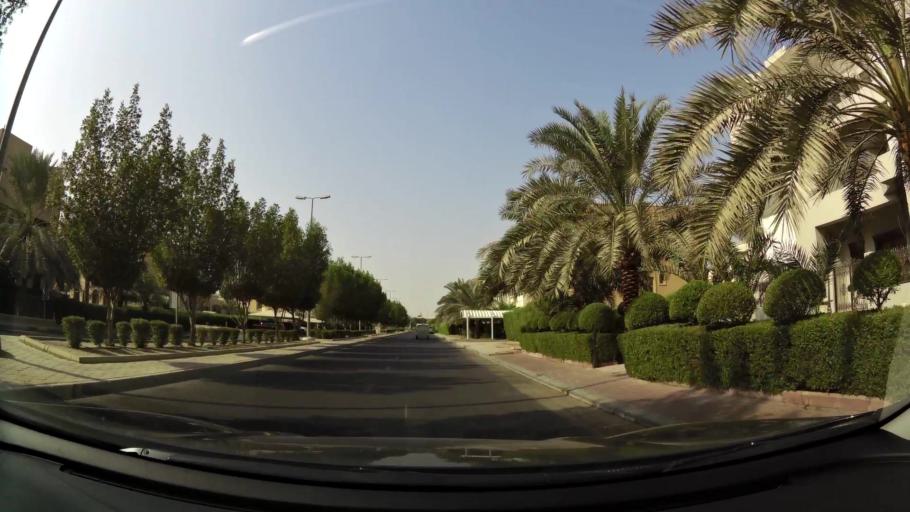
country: KW
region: Mubarak al Kabir
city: Sabah as Salim
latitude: 29.2781
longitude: 48.0432
